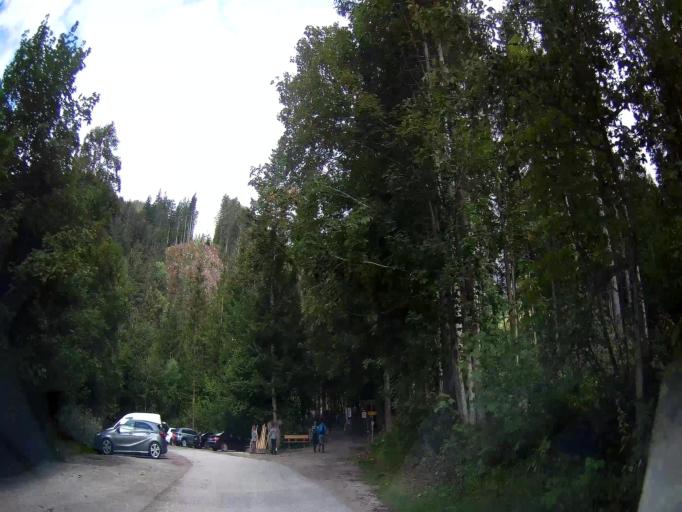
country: AT
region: Salzburg
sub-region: Politischer Bezirk Zell am See
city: Leogang
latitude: 47.4526
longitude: 12.7561
